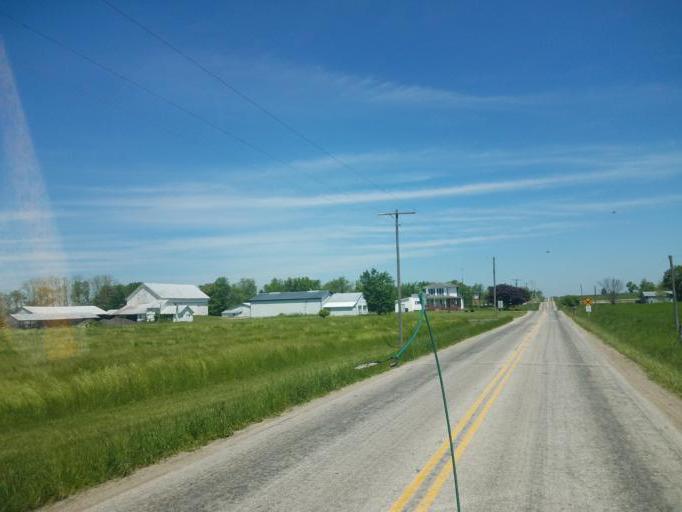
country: US
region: Ohio
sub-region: Ashland County
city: Ashland
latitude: 40.9313
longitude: -82.2433
